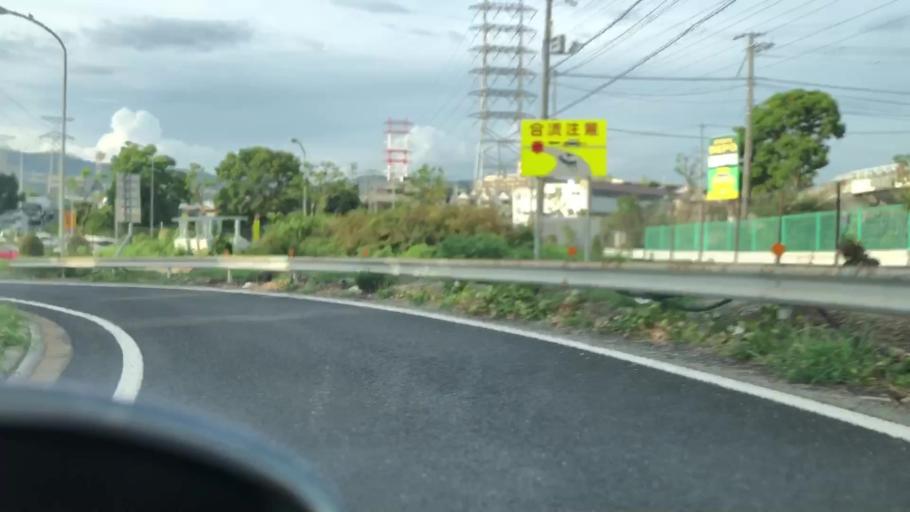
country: JP
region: Hyogo
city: Takarazuka
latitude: 34.8028
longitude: 135.3680
